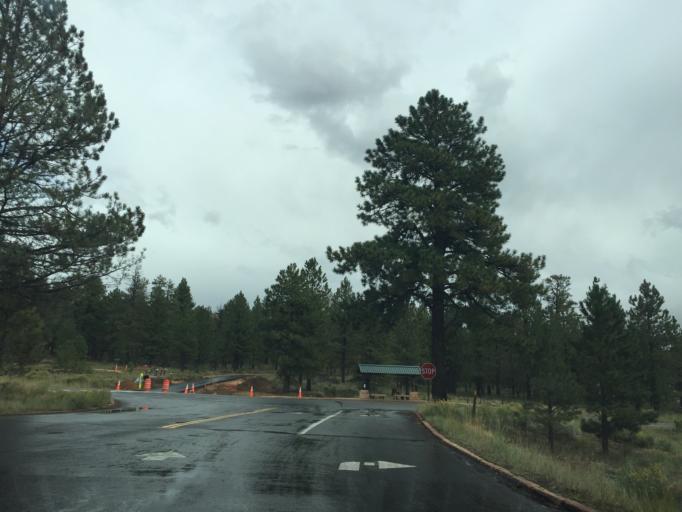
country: US
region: Utah
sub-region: Garfield County
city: Panguitch
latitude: 37.6398
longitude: -112.1702
